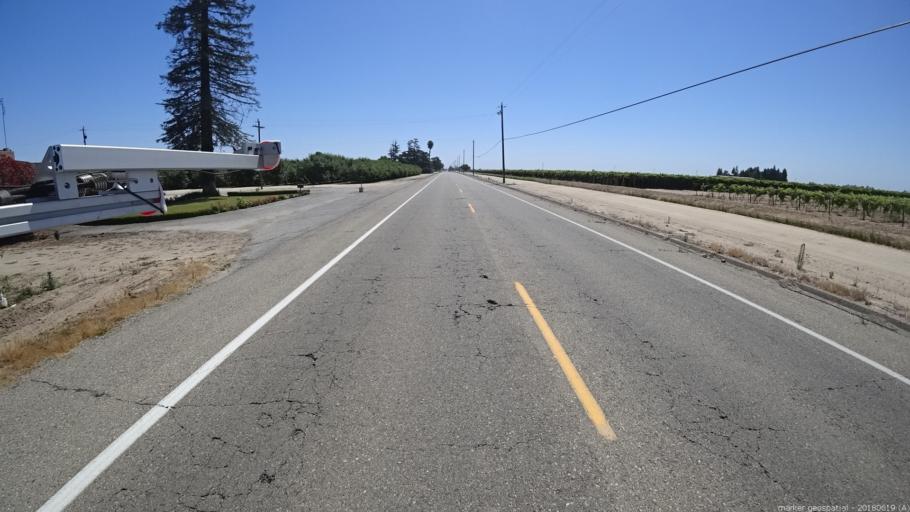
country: US
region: California
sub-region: Fresno County
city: Biola
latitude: 36.8513
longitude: -120.0792
